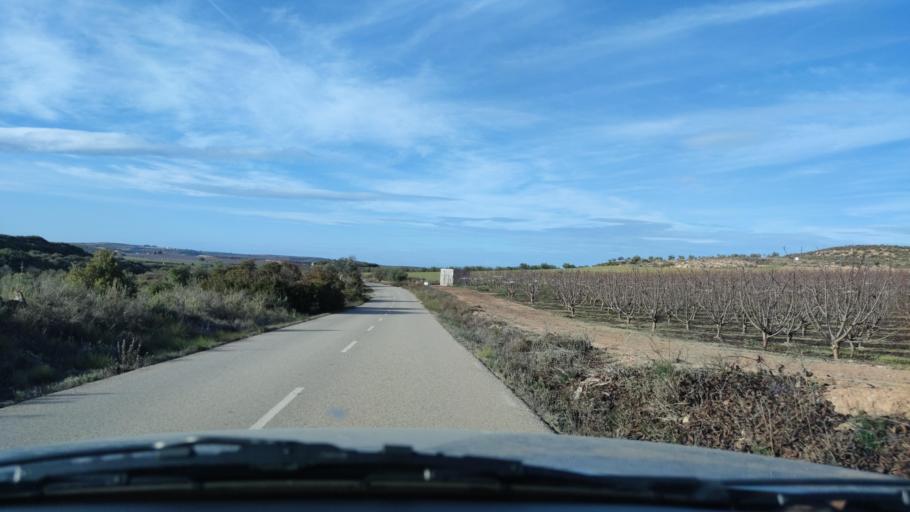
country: ES
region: Catalonia
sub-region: Provincia de Lleida
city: el Cogul
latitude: 41.4687
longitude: 0.6579
